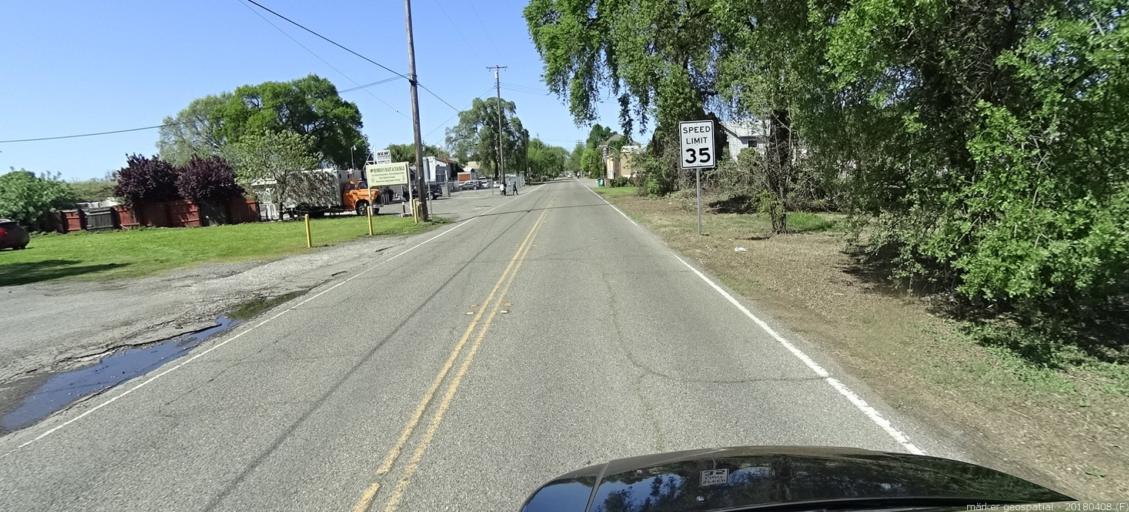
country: US
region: California
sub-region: Sacramento County
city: Parkway
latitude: 38.4608
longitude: -121.5016
